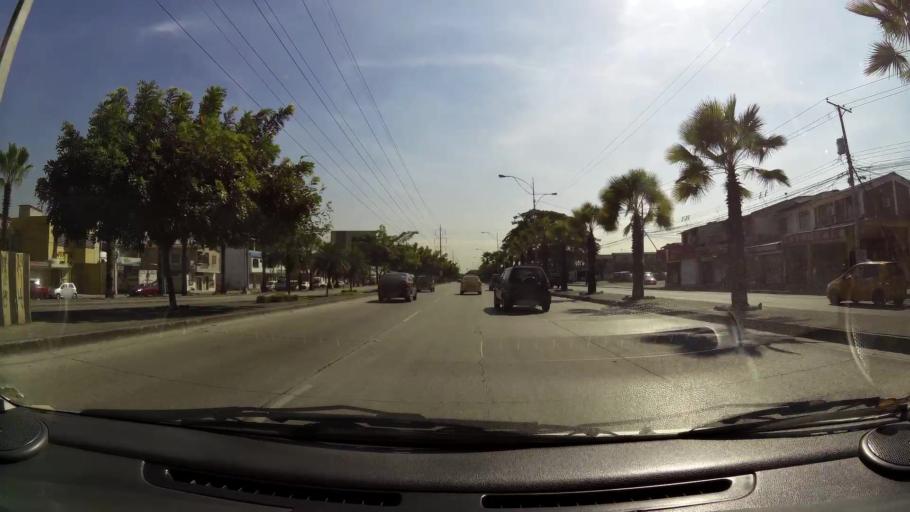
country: EC
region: Guayas
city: Eloy Alfaro
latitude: -2.1311
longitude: -79.9069
